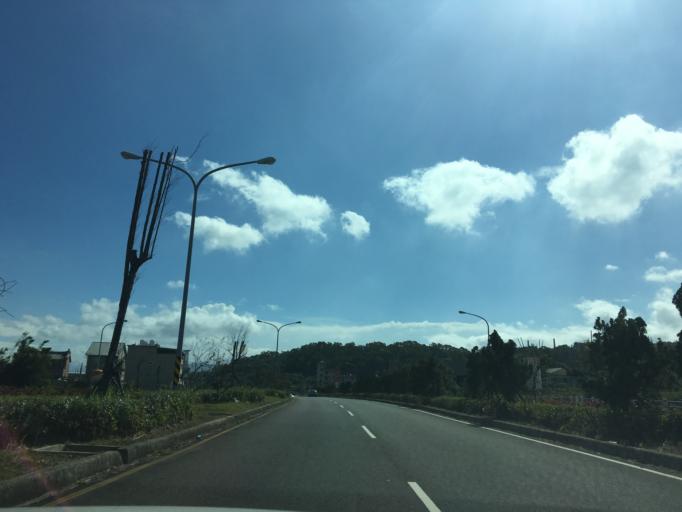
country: TW
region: Taiwan
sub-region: Hsinchu
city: Zhubei
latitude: 24.7826
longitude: 121.0398
